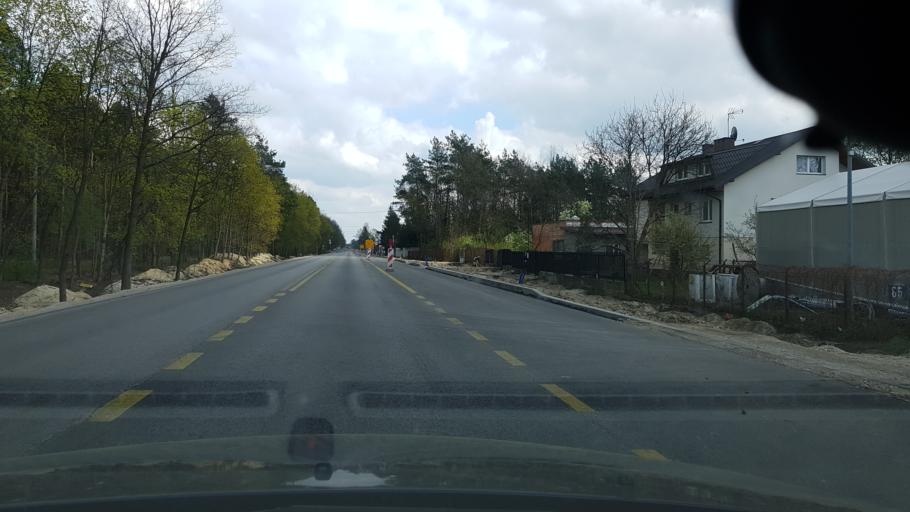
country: PL
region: Masovian Voivodeship
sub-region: Powiat minski
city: Sulejowek
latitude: 52.2527
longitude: 21.2624
